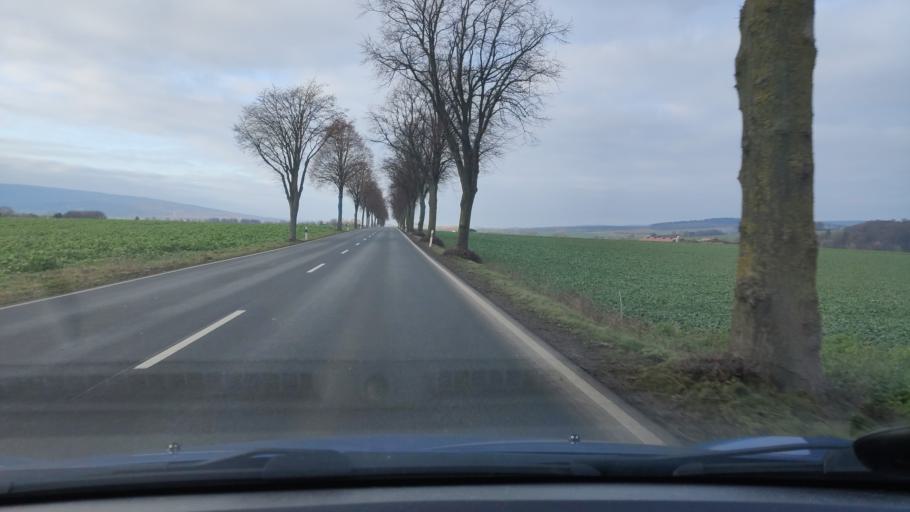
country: DE
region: Lower Saxony
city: Coppenbrugge
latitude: 52.1446
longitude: 9.5113
